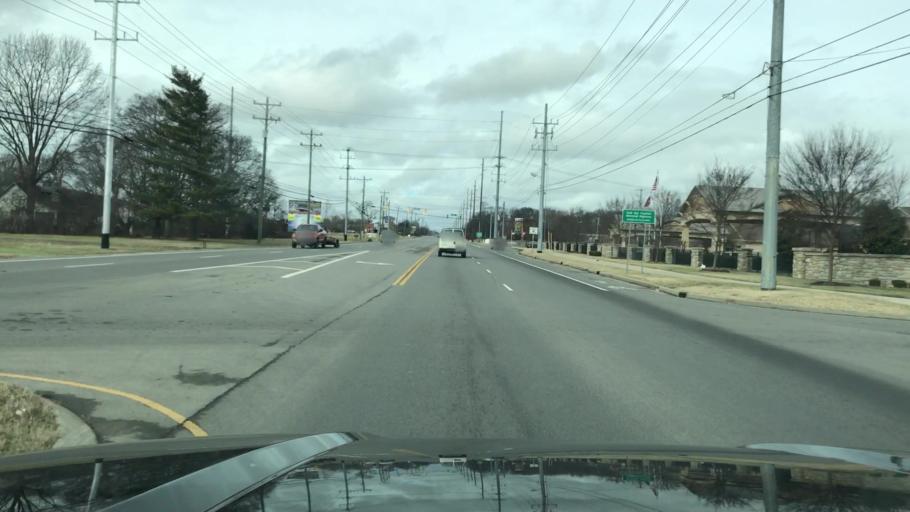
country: US
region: Tennessee
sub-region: Rutherford County
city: La Vergne
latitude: 36.0272
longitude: -86.5892
